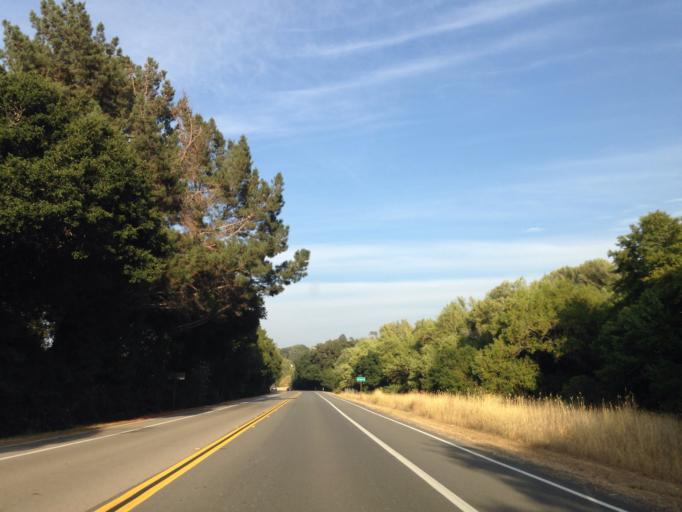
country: US
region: California
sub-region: Marin County
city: Lucas Valley-Marinwood
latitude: 38.0256
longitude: -122.5615
